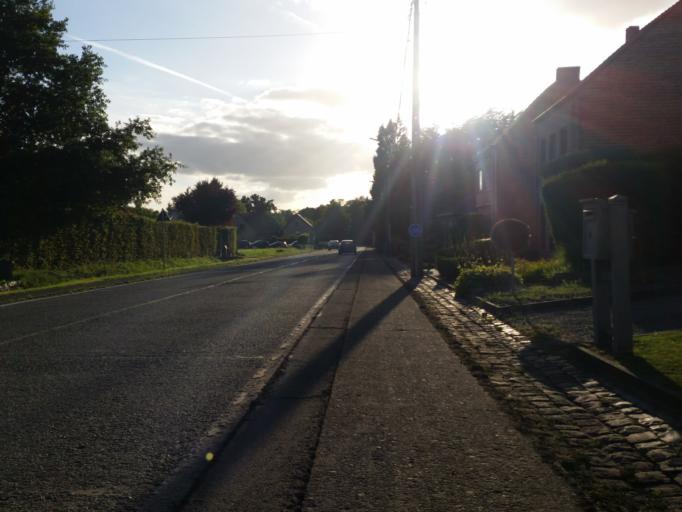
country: BE
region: Flanders
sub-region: Provincie Antwerpen
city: Duffel
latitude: 51.0704
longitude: 4.4790
